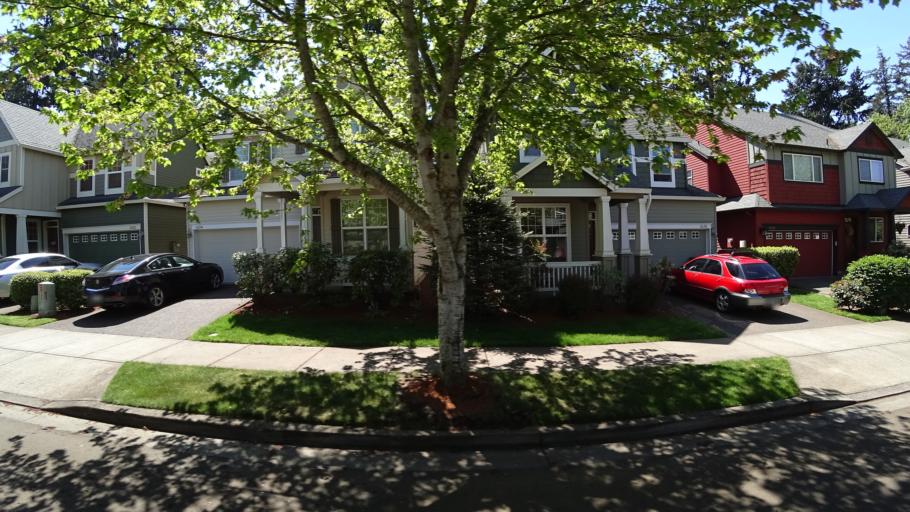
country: US
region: Oregon
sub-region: Washington County
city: Hillsboro
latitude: 45.5074
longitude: -122.9751
